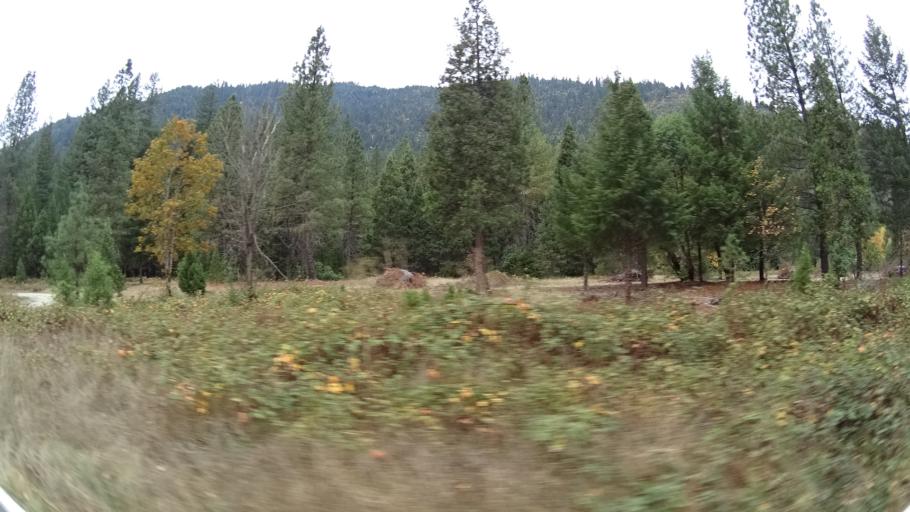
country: US
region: California
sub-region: Siskiyou County
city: Happy Camp
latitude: 41.8780
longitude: -123.4194
